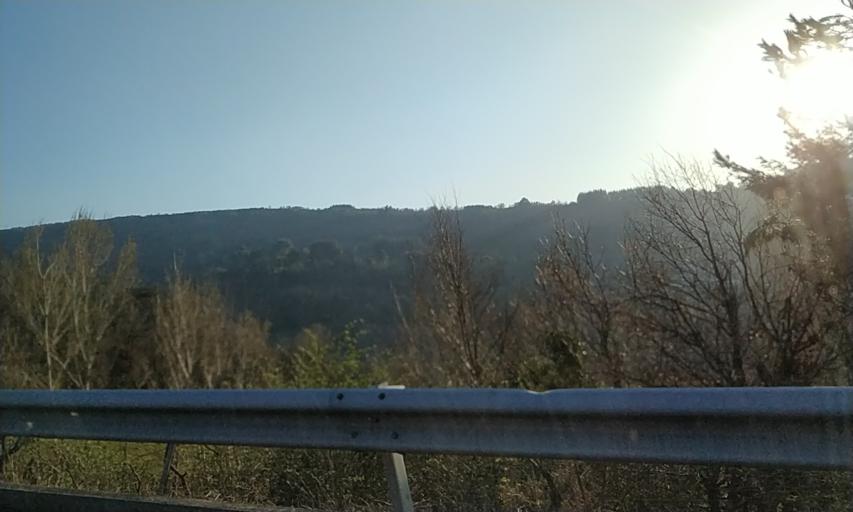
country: ES
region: Galicia
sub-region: Provincia de Lugo
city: Becerrea
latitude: 42.8930
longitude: -7.1844
